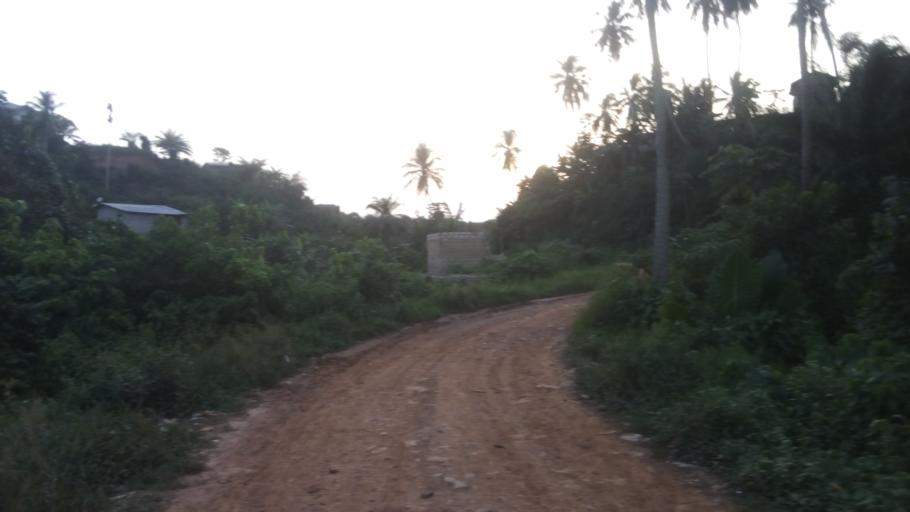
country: GH
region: Western
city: Tarkwa
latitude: 5.3092
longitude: -1.9975
